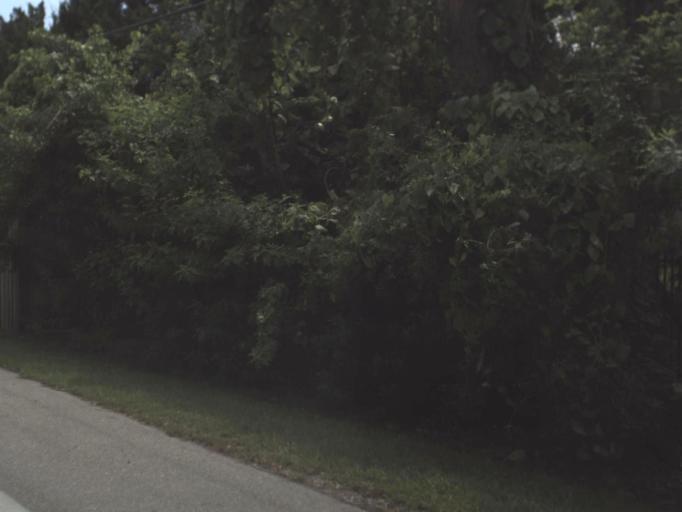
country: US
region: Florida
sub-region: Sarasota County
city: South Sarasota
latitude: 27.2784
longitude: -82.5502
